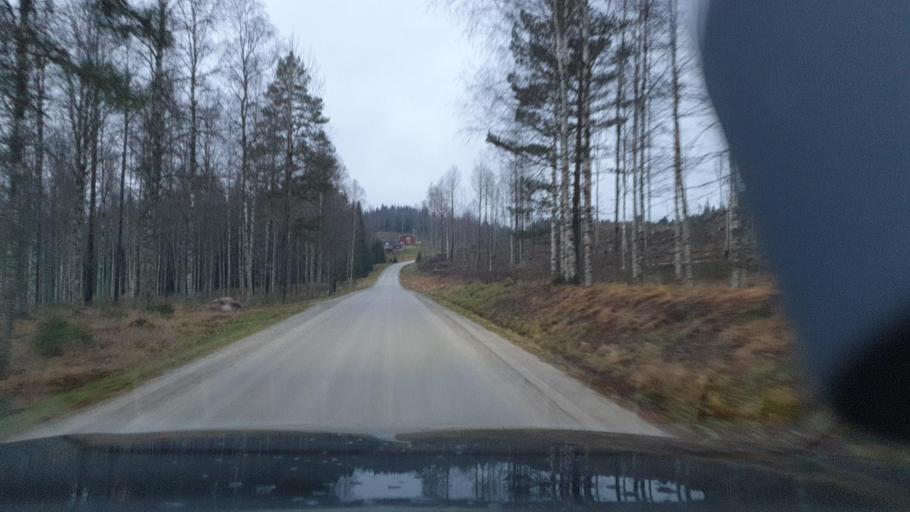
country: SE
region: Vaermland
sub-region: Arvika Kommun
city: Arvika
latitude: 59.8293
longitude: 12.7472
